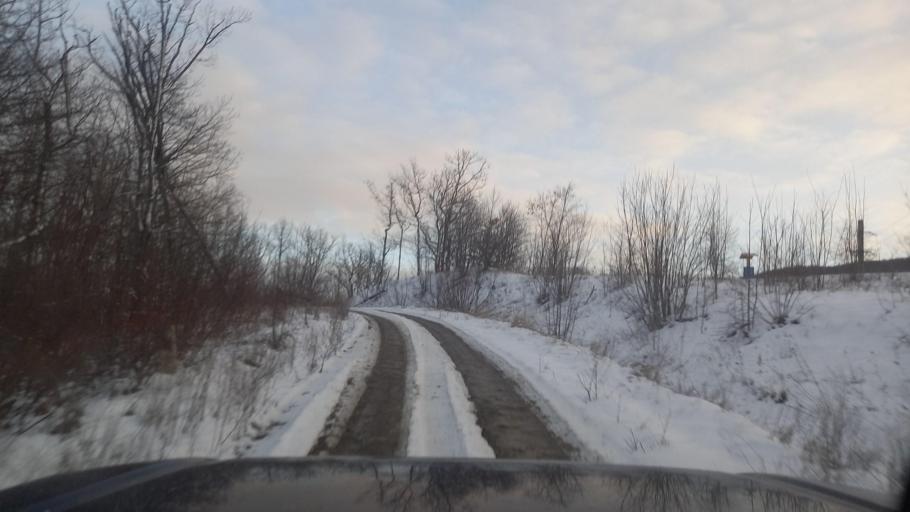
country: RU
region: Krasnodarskiy
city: Smolenskaya
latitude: 44.6759
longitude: 38.7964
